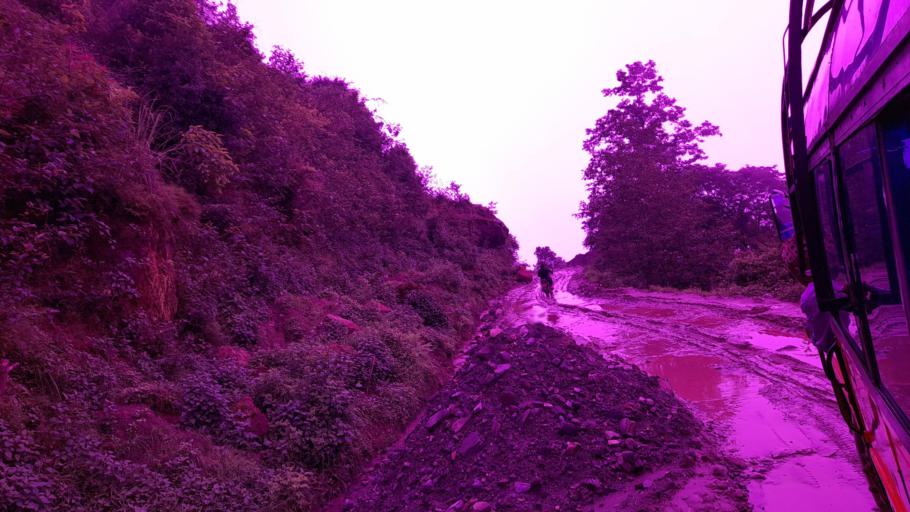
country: NP
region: Central Region
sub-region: Bagmati Zone
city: Kathmandu
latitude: 27.8306
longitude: 85.2357
